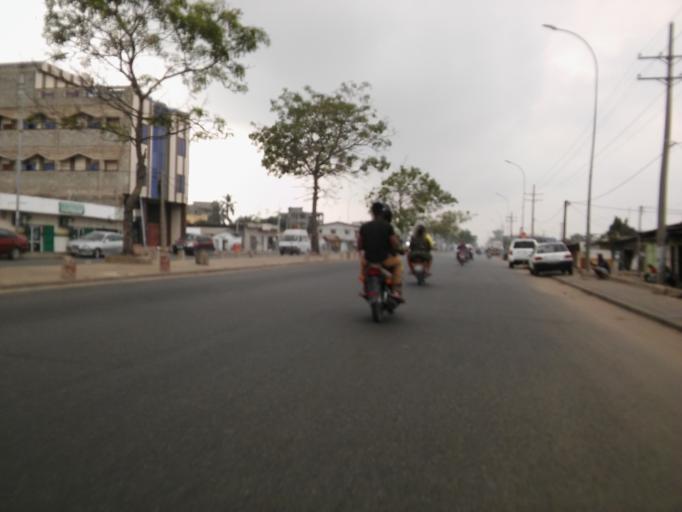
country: BJ
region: Littoral
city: Cotonou
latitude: 6.3767
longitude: 2.3995
